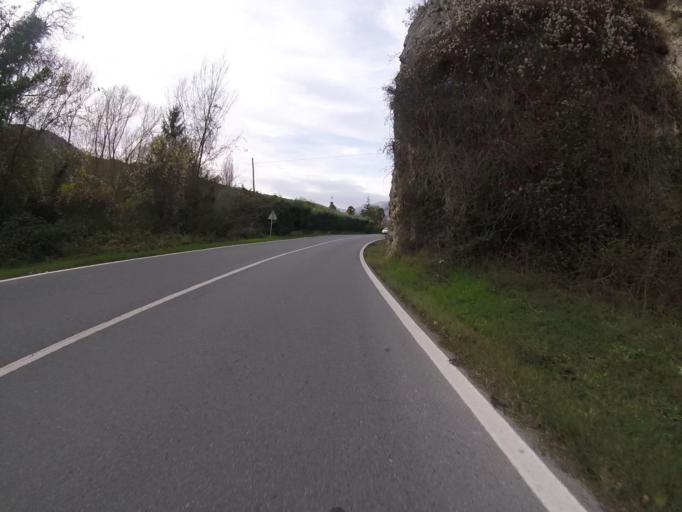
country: ES
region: Navarre
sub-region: Provincia de Navarra
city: Estella
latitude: 42.7014
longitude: -2.0586
